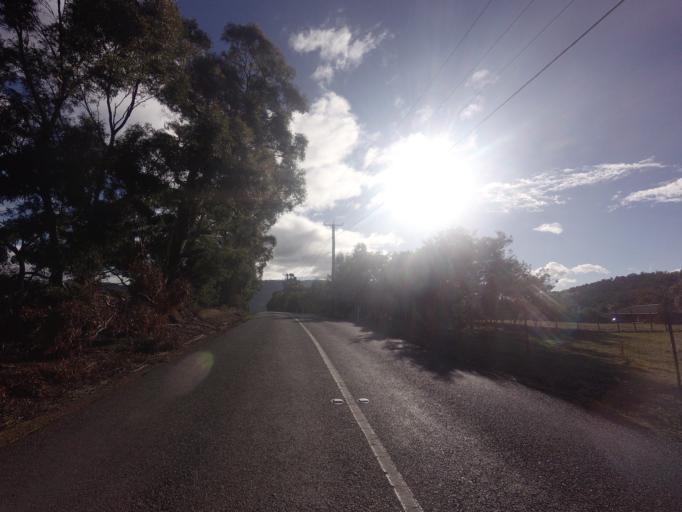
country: AU
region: Tasmania
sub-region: Derwent Valley
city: New Norfolk
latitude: -42.7906
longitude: 147.1227
